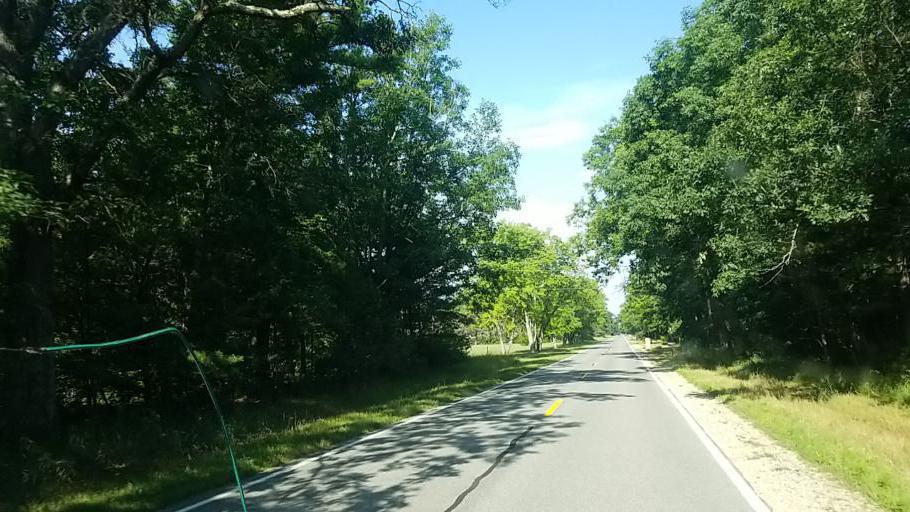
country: US
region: Michigan
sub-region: Muskegon County
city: Twin Lake
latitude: 43.4685
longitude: -86.1478
